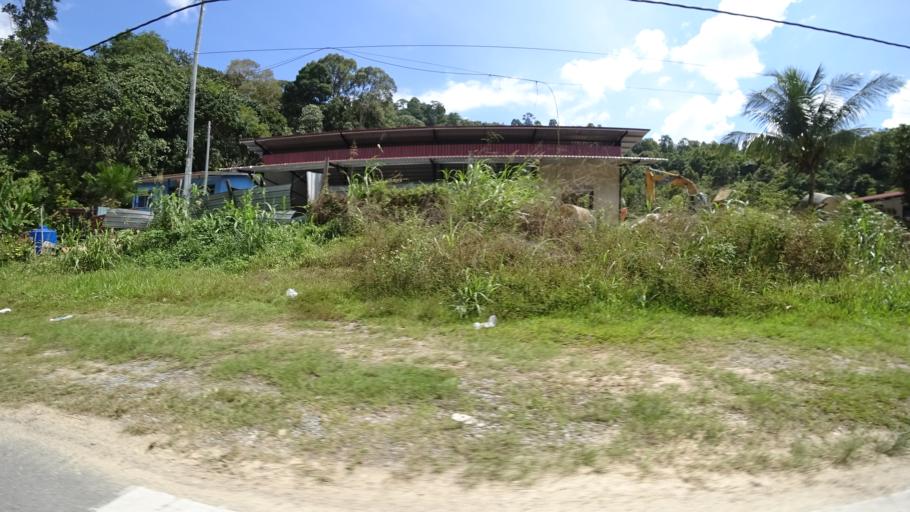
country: MY
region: Sarawak
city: Limbang
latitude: 4.6735
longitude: 114.9836
